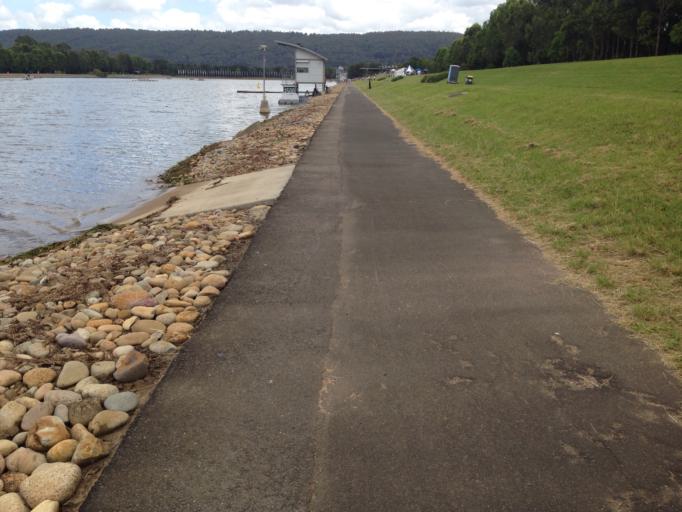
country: AU
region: New South Wales
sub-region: Penrith Municipality
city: Emu Heights
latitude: -33.7237
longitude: 150.6771
